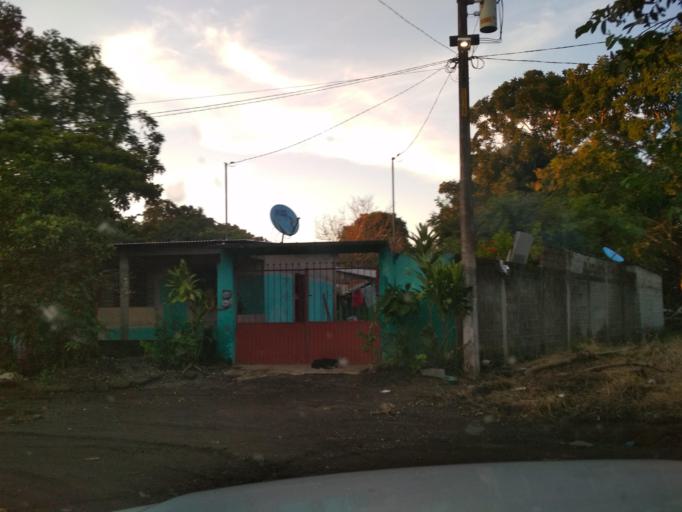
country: MX
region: Veracruz
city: Catemaco
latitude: 18.4188
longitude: -95.1009
